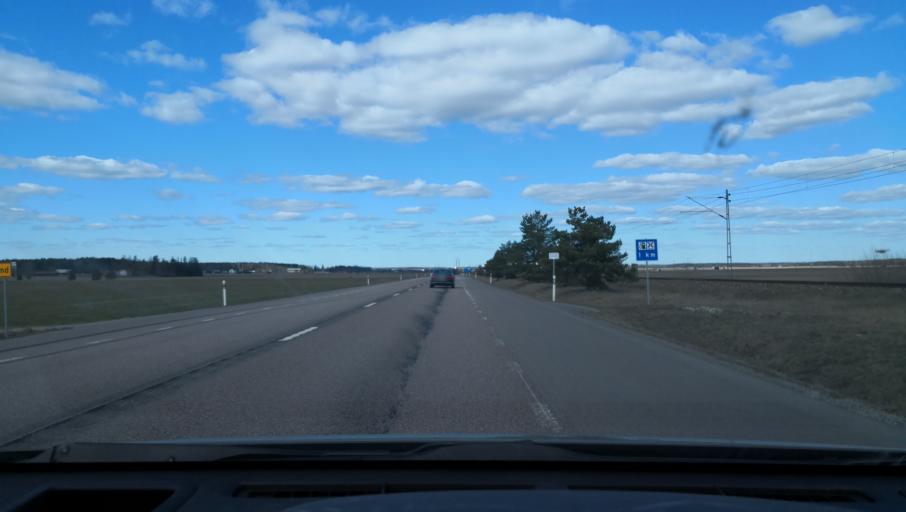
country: SE
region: Vaestmanland
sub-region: Sala Kommun
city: Sala
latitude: 59.8787
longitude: 16.6257
